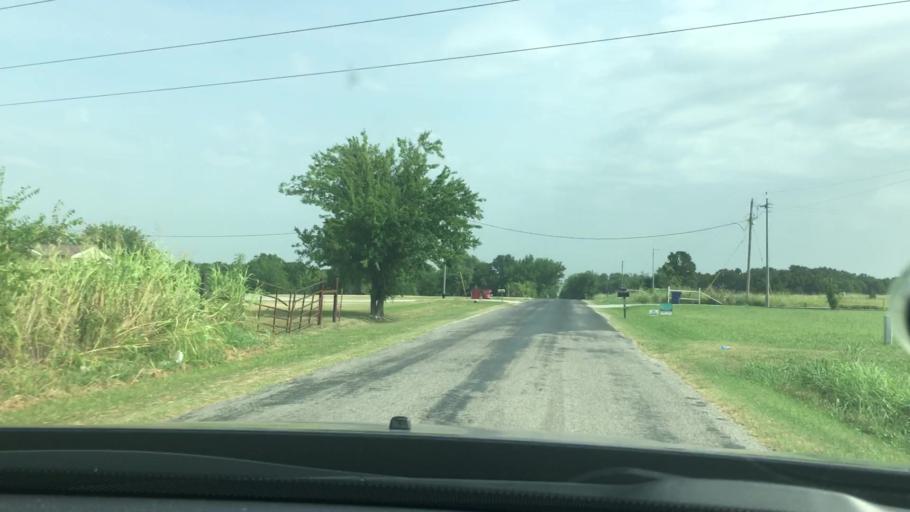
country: US
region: Oklahoma
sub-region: Garvin County
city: Pauls Valley
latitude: 34.8055
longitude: -97.1955
